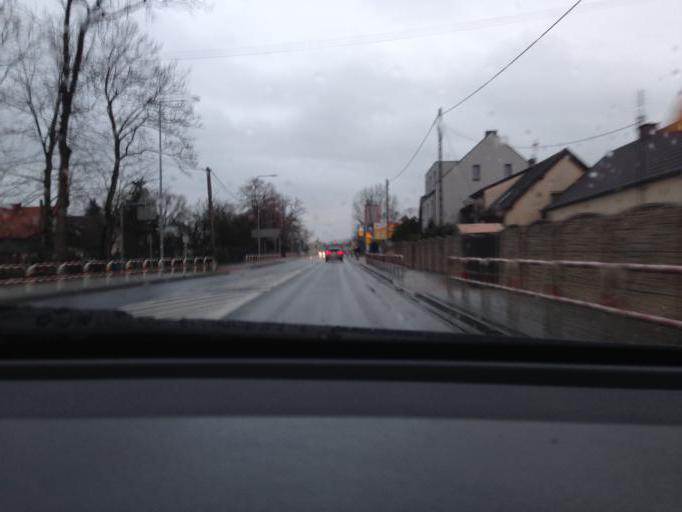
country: PL
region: Opole Voivodeship
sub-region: Powiat opolski
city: Wegry
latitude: 50.7134
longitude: 17.9930
